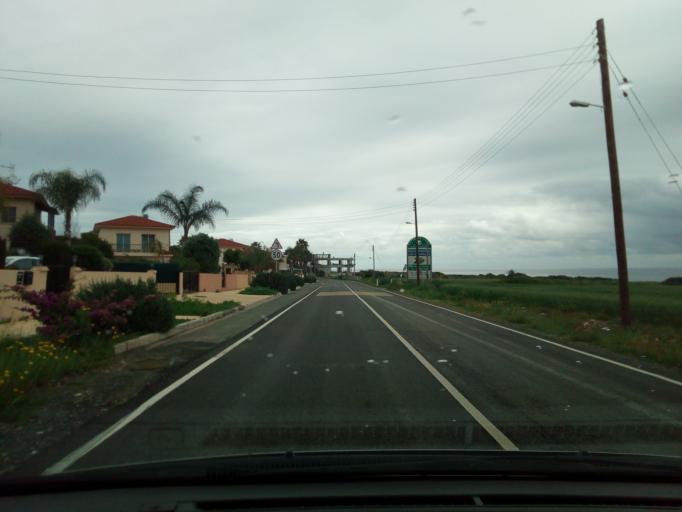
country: CY
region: Larnaka
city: Kofinou
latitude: 34.7332
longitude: 33.3511
